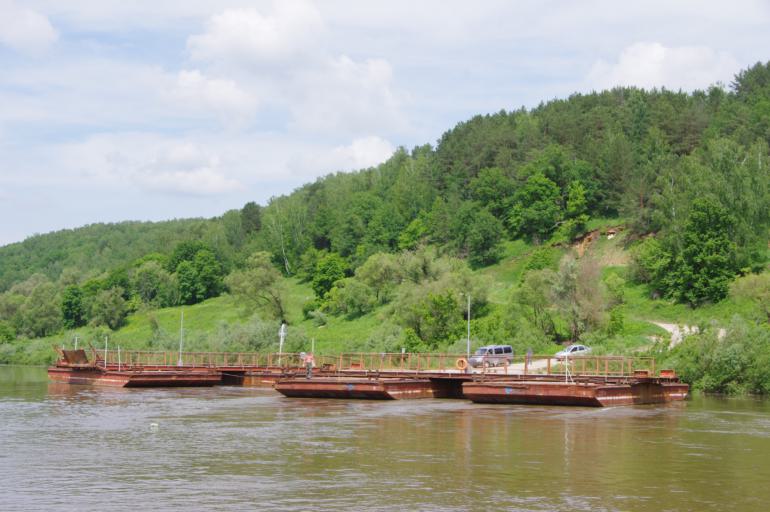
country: RU
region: Kaluga
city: Ferzikovo
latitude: 54.4274
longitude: 36.8619
